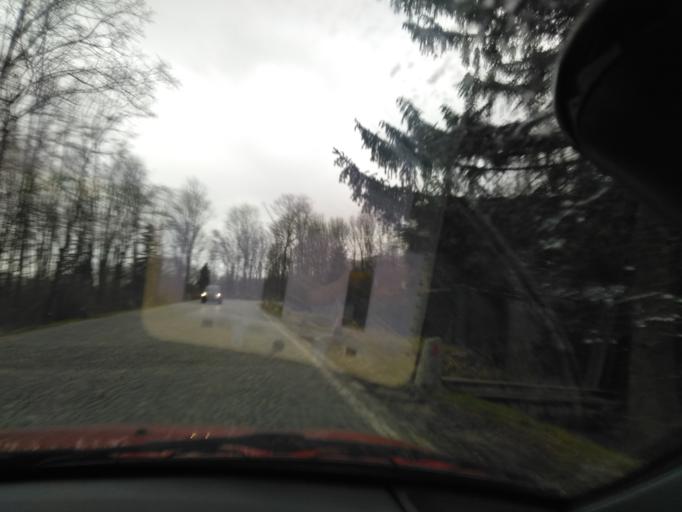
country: AT
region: Lower Austria
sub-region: Politischer Bezirk Wien-Umgebung
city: Klosterneuburg
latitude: 48.2512
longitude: 16.2752
